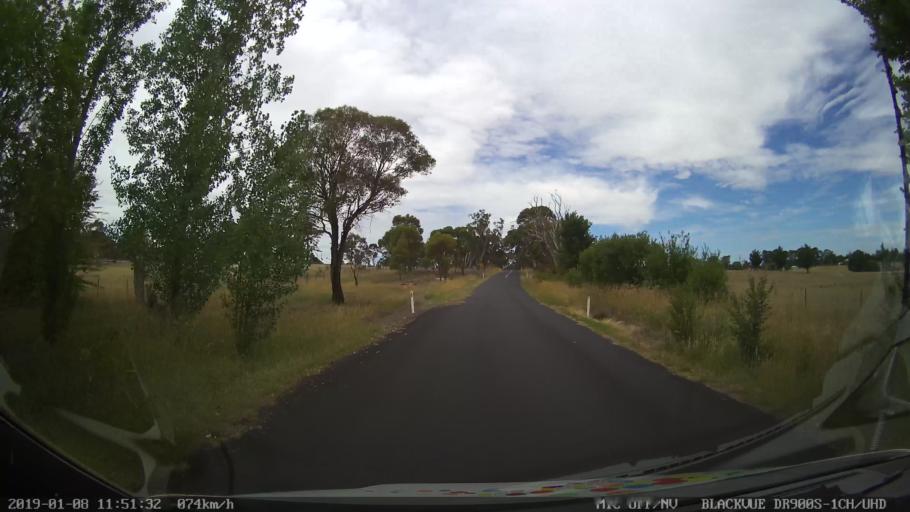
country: AU
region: New South Wales
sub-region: Armidale Dumaresq
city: Armidale
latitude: -30.3940
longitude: 151.5604
